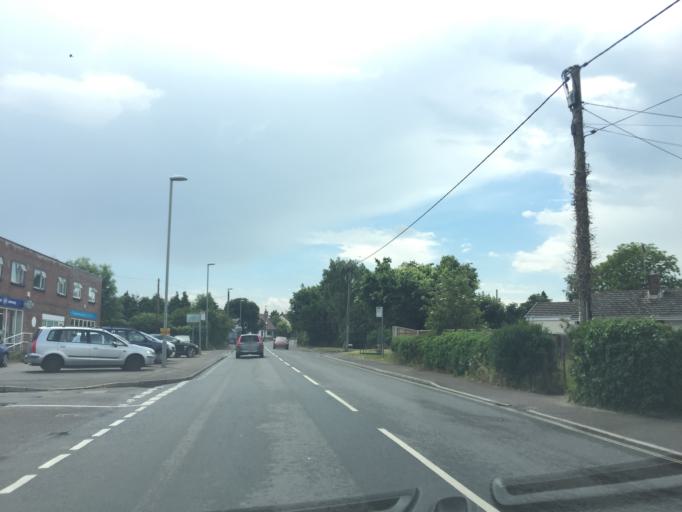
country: GB
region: England
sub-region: Dorset
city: Wool
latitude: 50.6790
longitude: -2.2285
